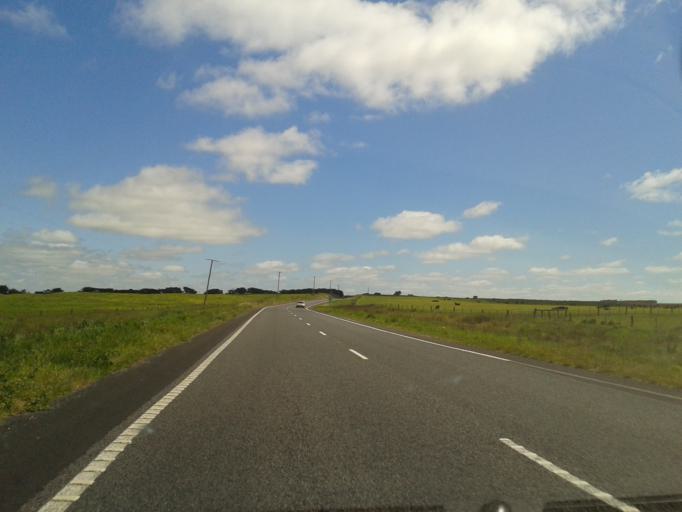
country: AU
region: Victoria
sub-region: Moyne
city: Port Fairy
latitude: -38.2935
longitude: 142.0194
